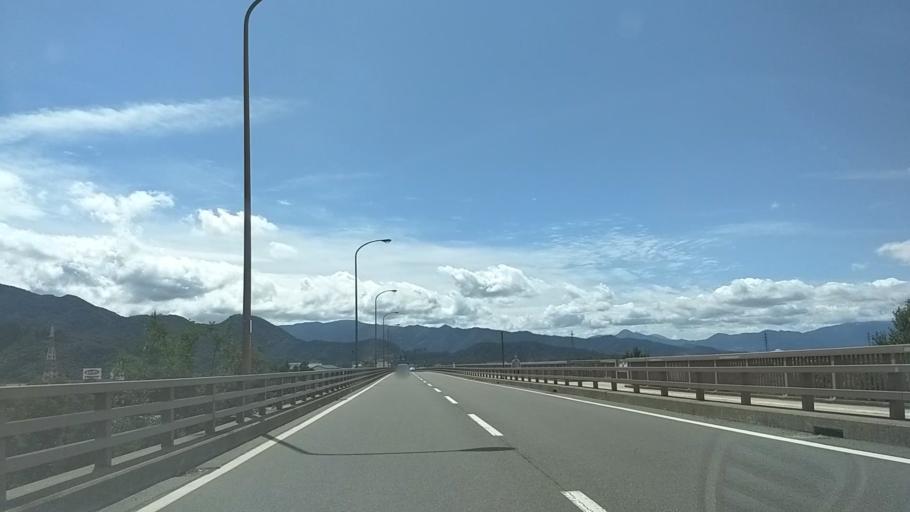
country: JP
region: Nagano
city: Nagano-shi
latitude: 36.6211
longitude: 138.2248
